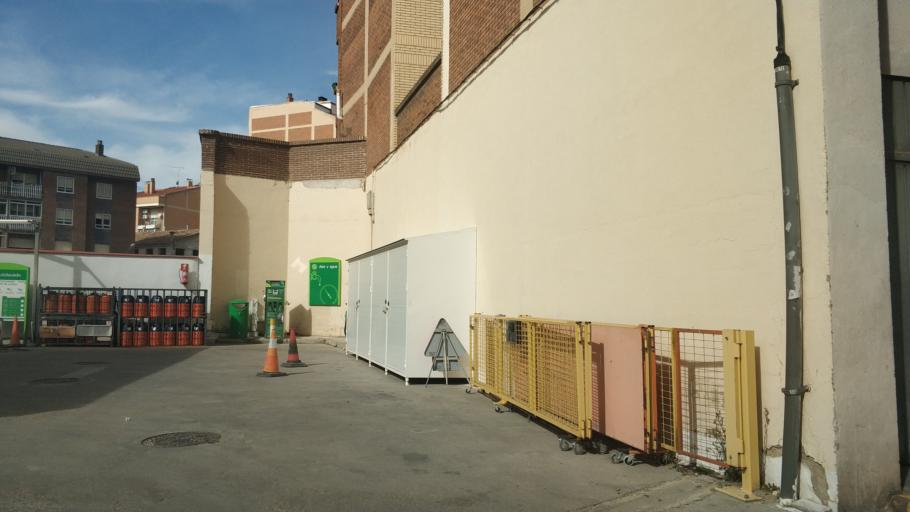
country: ES
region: Castille and Leon
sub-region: Provincia de Burgos
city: Aranda de Duero
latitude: 41.6751
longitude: -3.6860
